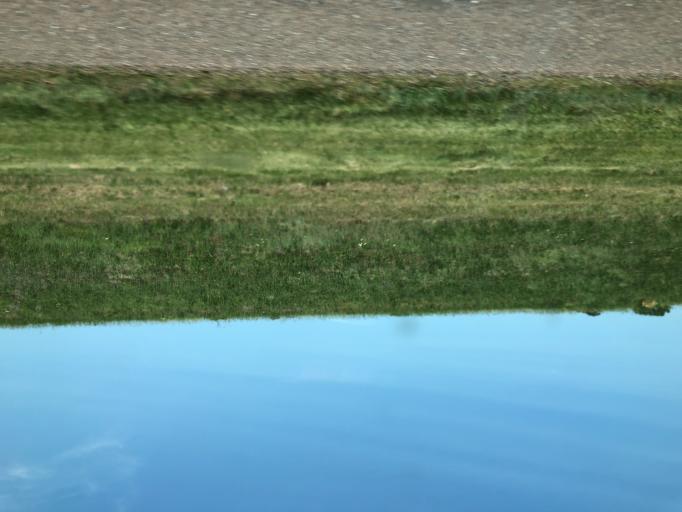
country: US
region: Nebraska
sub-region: Thayer County
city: Hebron
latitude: 40.1805
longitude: -97.5747
